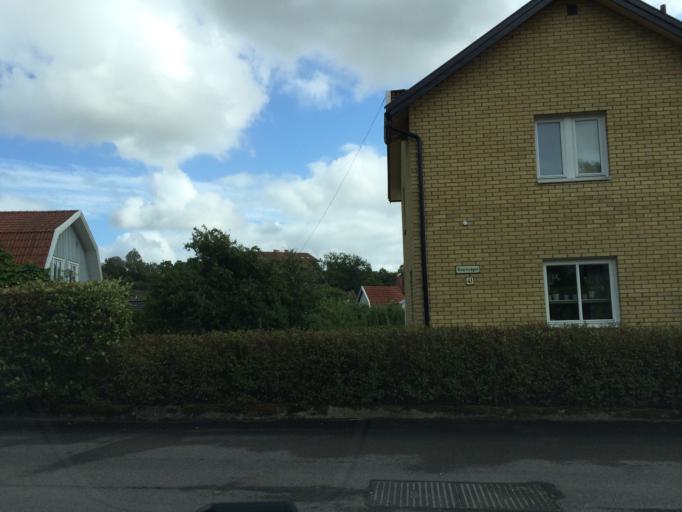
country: SE
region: Vaestra Goetaland
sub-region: Trollhattan
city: Trollhattan
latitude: 58.2858
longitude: 12.2685
